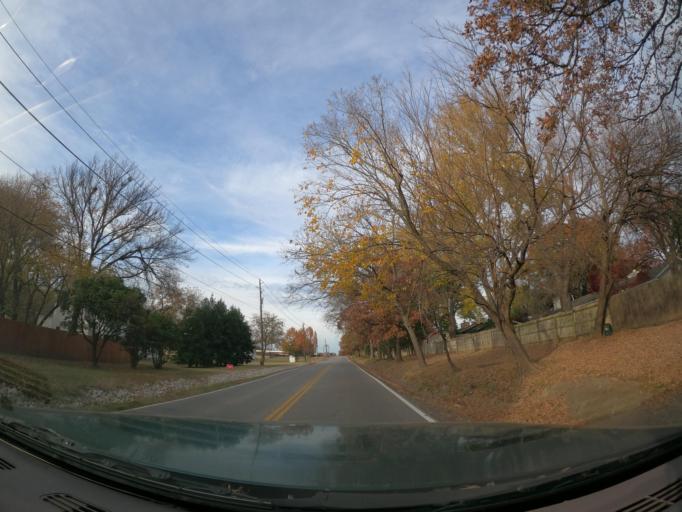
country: US
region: Oklahoma
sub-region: Tulsa County
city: Jenks
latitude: 36.0416
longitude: -95.9400
